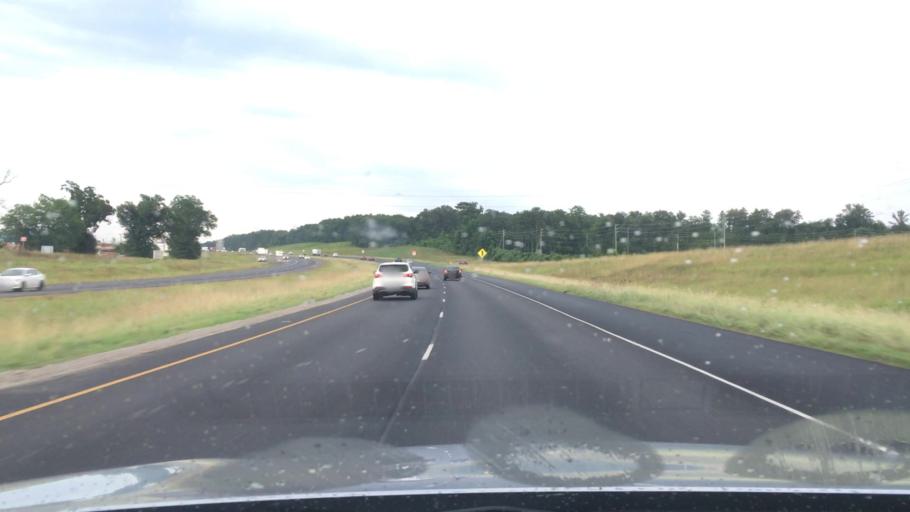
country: US
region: Alabama
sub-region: Jefferson County
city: Bessemer
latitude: 33.3324
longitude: -86.9975
